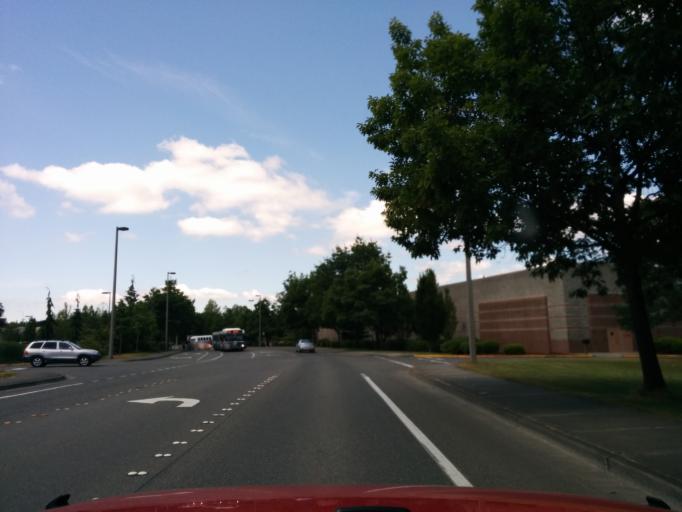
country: US
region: Washington
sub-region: King County
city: Redmond
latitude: 47.6716
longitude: -122.1020
